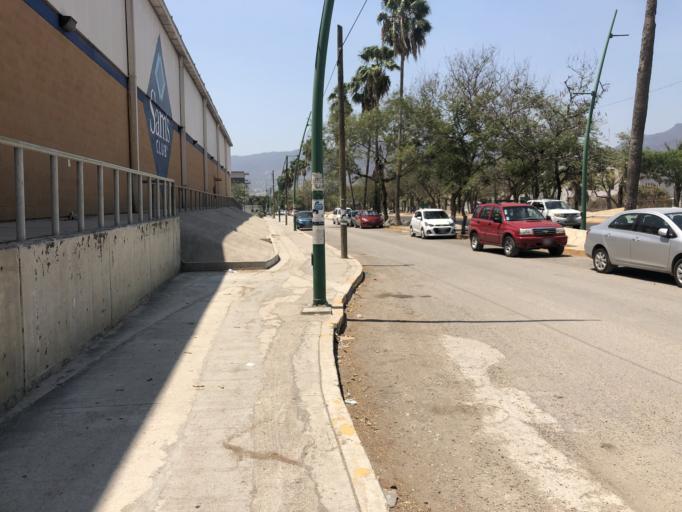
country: MX
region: Chiapas
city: Tuxtla Gutierrez
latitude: 16.7463
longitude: -93.0734
